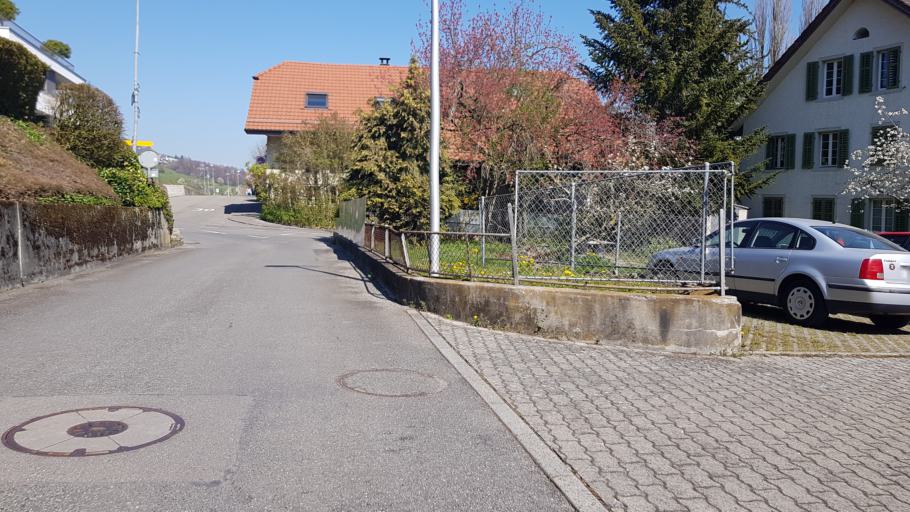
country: CH
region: Aargau
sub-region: Bezirk Kulm
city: Reinach
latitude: 47.2682
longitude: 8.2095
